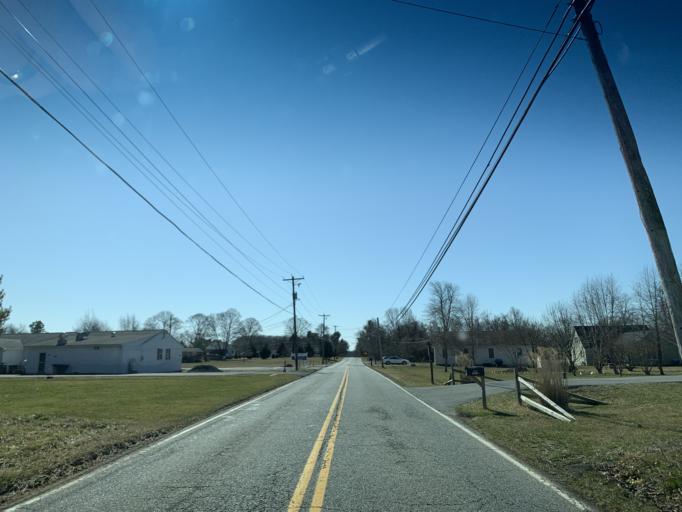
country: US
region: Maryland
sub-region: Cecil County
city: Rising Sun
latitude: 39.6311
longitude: -76.0770
